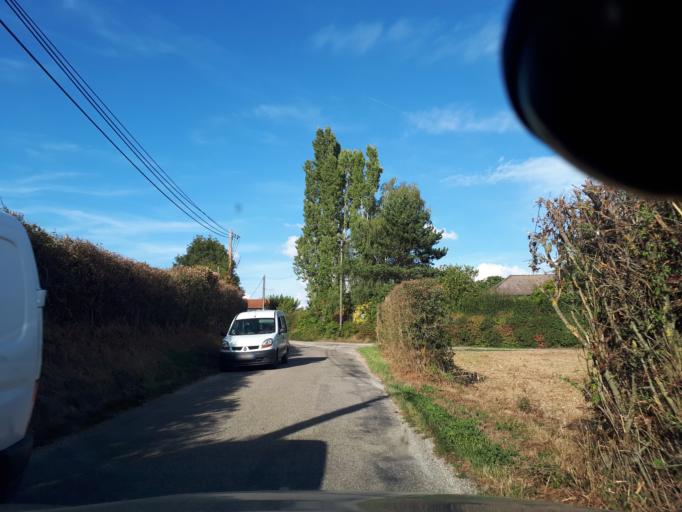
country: FR
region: Rhone-Alpes
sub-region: Departement de l'Isere
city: Maubec
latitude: 45.5217
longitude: 5.2517
